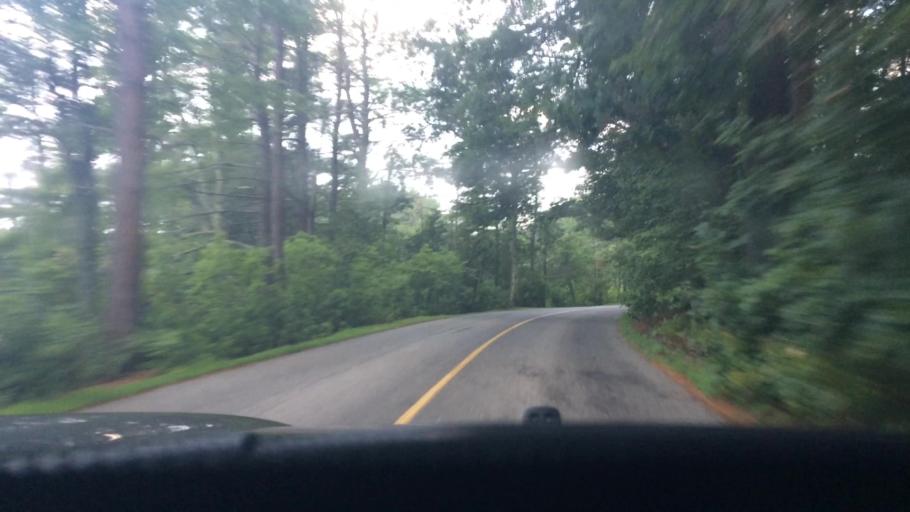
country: US
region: Massachusetts
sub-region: Middlesex County
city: North Reading
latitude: 42.6111
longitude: -71.1057
